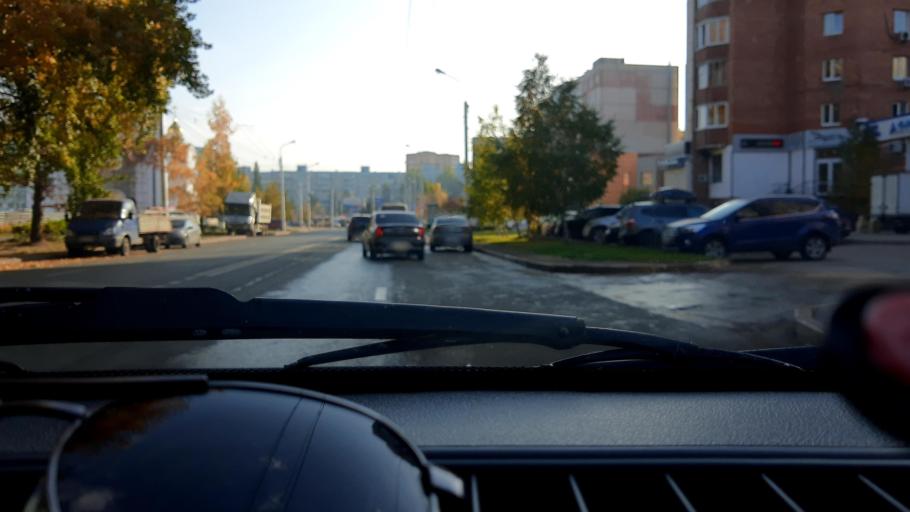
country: RU
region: Bashkortostan
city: Ufa
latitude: 54.7644
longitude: 56.0612
